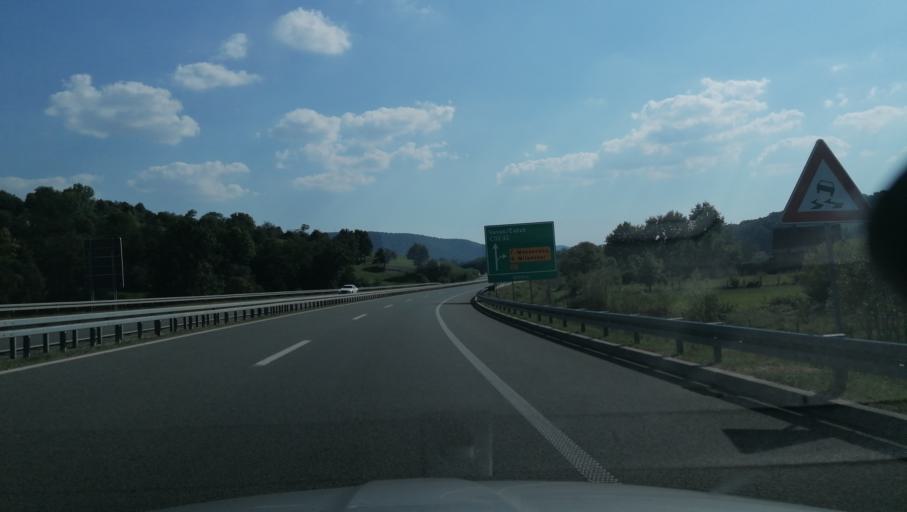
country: RS
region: Central Serbia
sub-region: Moravicki Okrug
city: Gornji Milanovac
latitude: 44.0596
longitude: 20.3817
